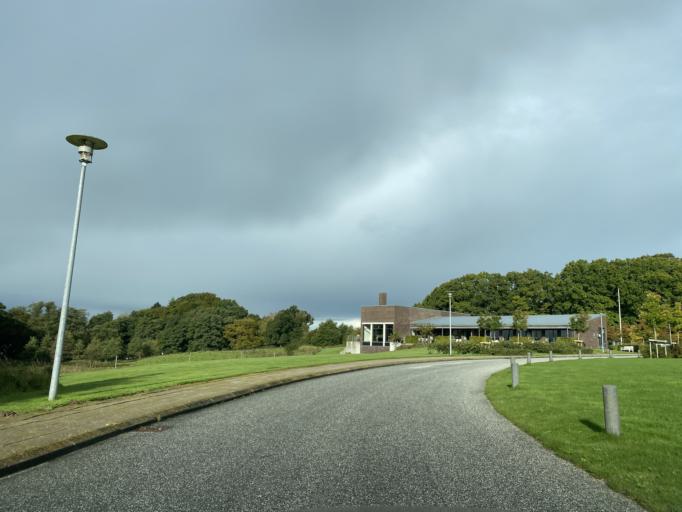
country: DK
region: South Denmark
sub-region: Haderslev Kommune
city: Haderslev
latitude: 55.2454
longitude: 9.4456
